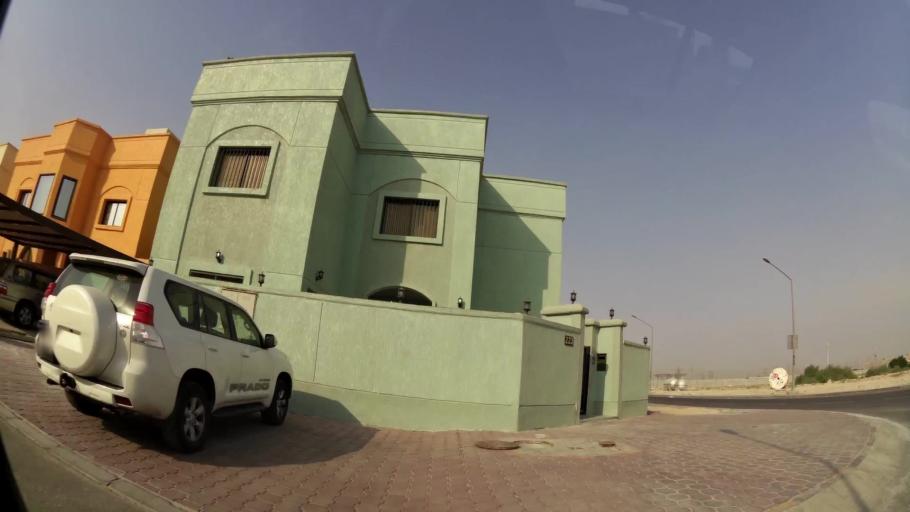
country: KW
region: Al Asimah
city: Ar Rabiyah
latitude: 29.3348
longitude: 47.8031
